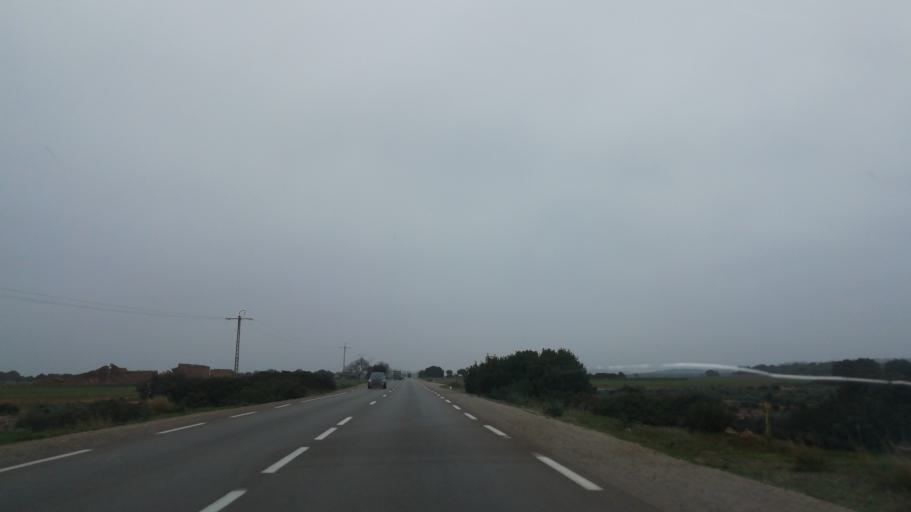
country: DZ
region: Mascara
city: Oued el Abtal
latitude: 35.3039
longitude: 0.4327
